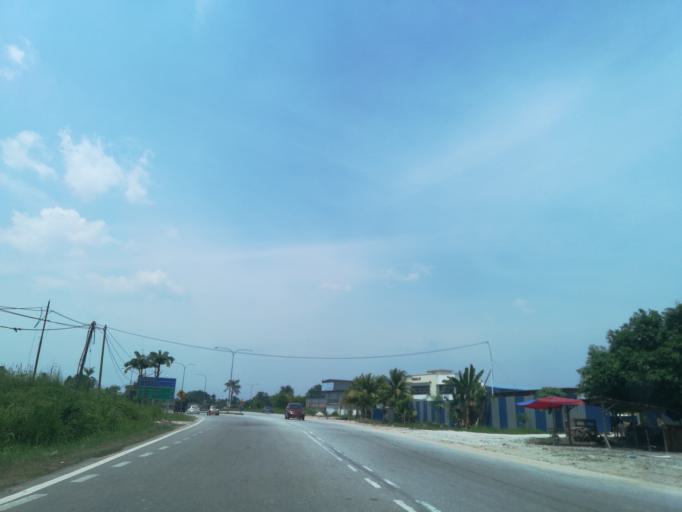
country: MY
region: Penang
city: Tasek Glugor
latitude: 5.4356
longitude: 100.5518
